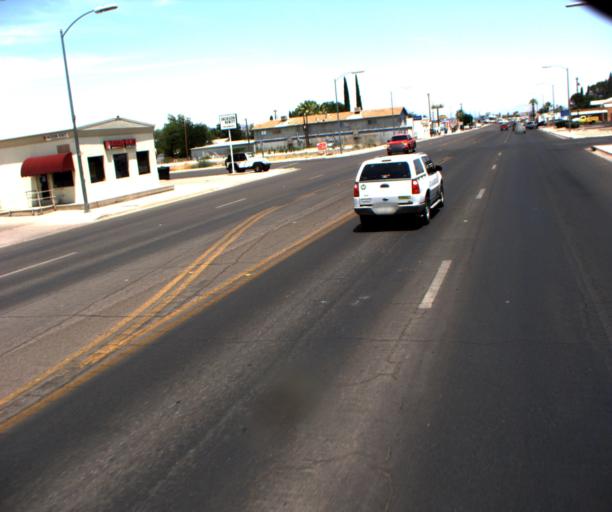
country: US
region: Arizona
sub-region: Graham County
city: Safford
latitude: 32.8343
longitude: -109.7119
